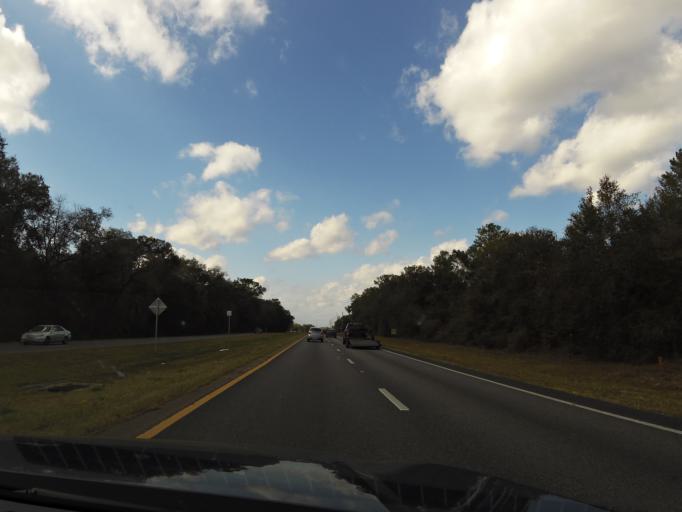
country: US
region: Florida
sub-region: Volusia County
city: North DeLand
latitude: 29.0737
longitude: -81.3080
